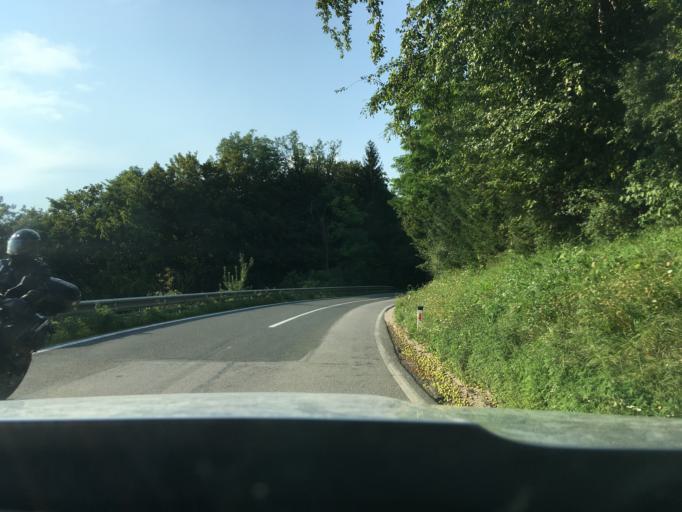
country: SI
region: Novo Mesto
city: Novo Mesto
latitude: 45.7524
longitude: 15.2000
